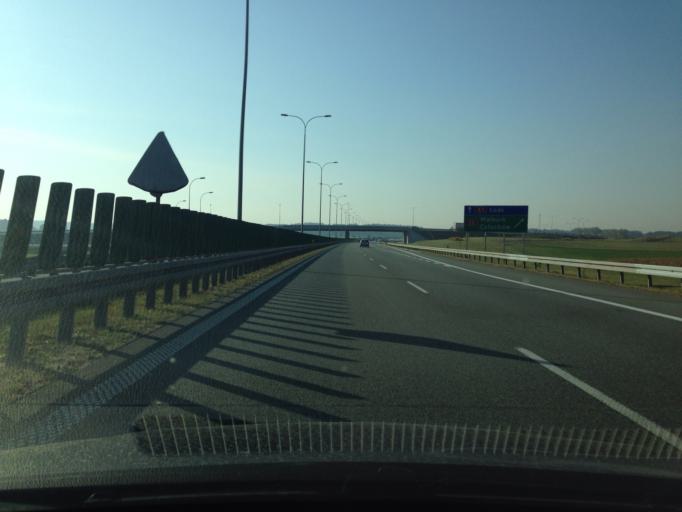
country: PL
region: Pomeranian Voivodeship
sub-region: Powiat tczewski
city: Subkowy
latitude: 54.0340
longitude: 18.6713
